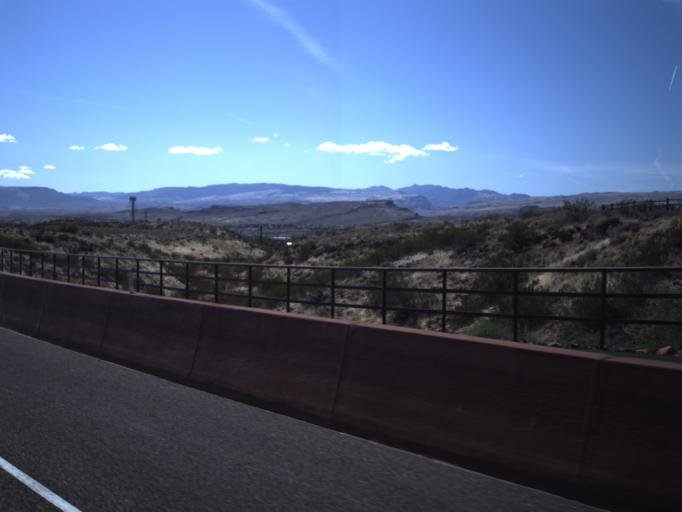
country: US
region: Utah
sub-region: Washington County
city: Saint George
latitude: 37.1378
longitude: -113.6034
